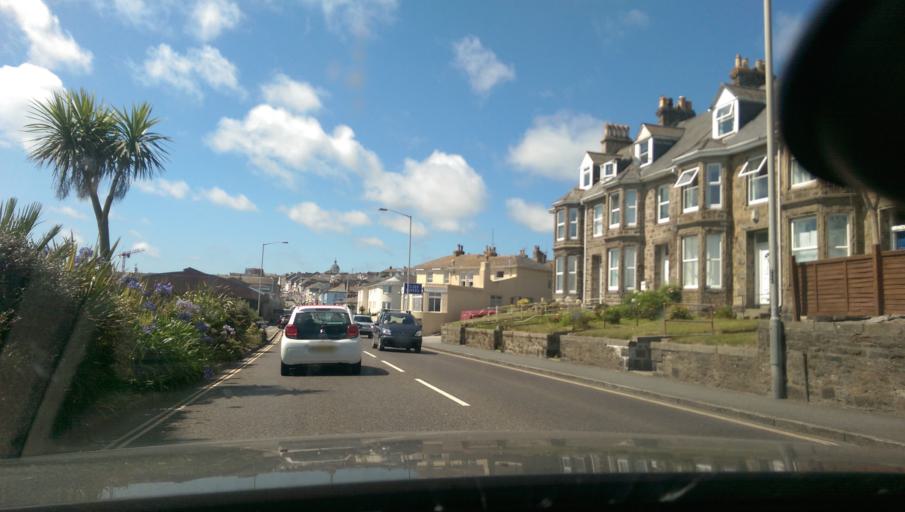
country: GB
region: England
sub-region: Cornwall
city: Penzance
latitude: 50.1233
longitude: -5.5316
